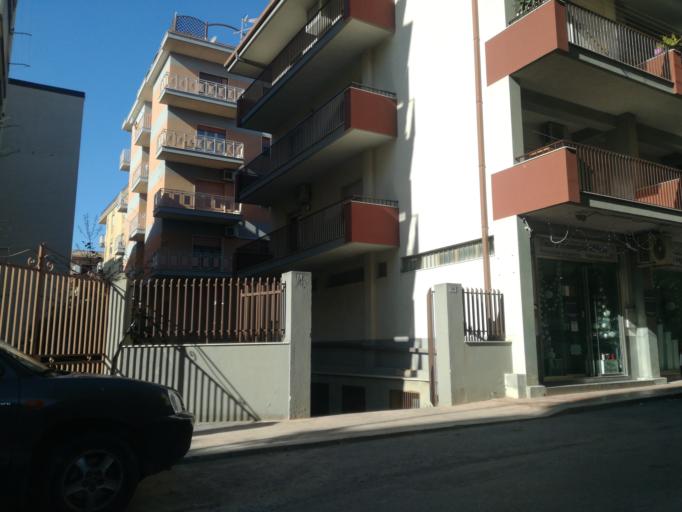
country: IT
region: Sicily
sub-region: Provincia di Caltanissetta
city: Gela
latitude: 37.0731
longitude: 14.2323
